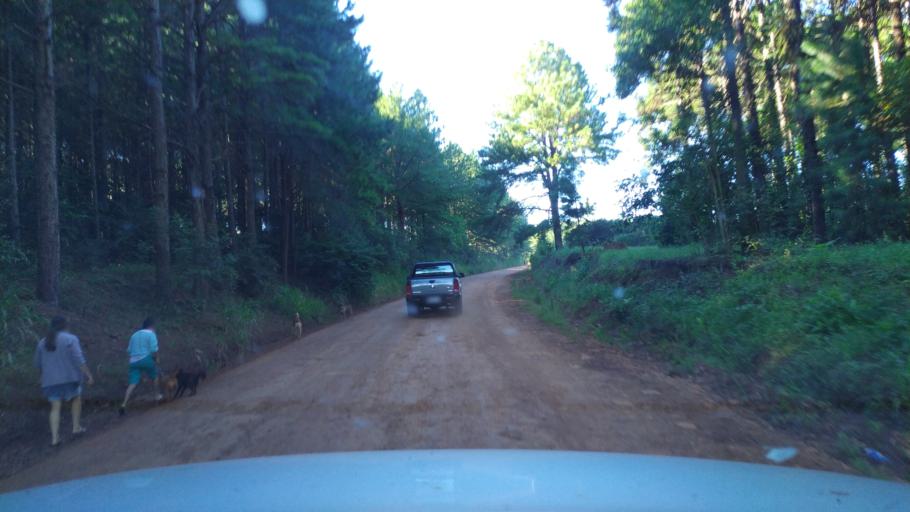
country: AR
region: Misiones
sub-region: Departamento de Montecarlo
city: Montecarlo
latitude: -26.6092
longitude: -54.6985
